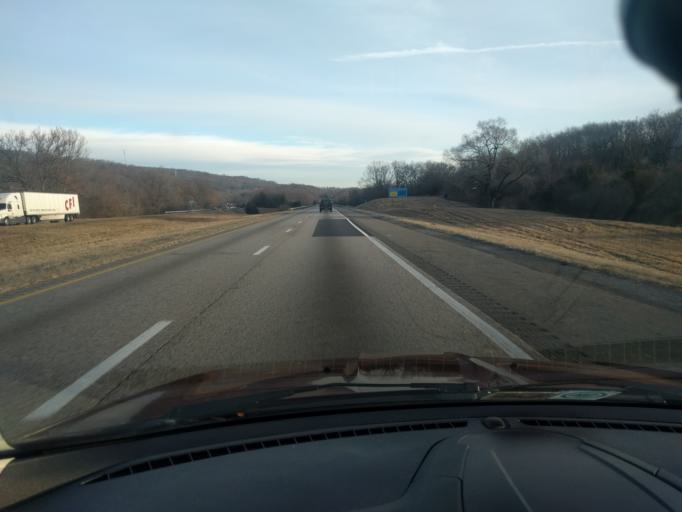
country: US
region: Virginia
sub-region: Augusta County
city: Jolivue
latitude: 38.0476
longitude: -79.1199
